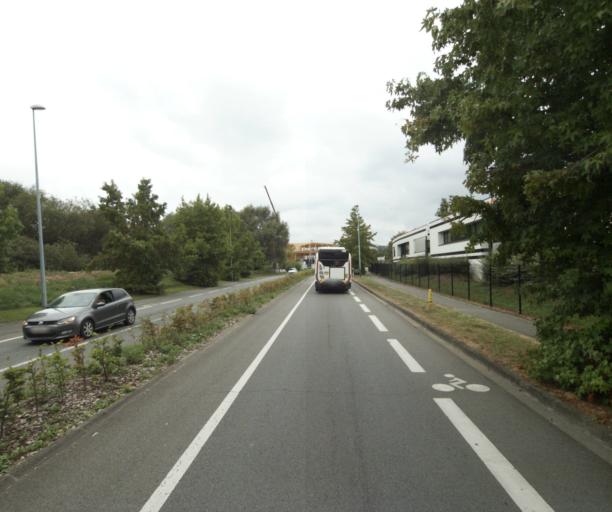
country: FR
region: Nord-Pas-de-Calais
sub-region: Departement du Nord
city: Mons-en-Baroeul
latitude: 50.6436
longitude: 3.1376
